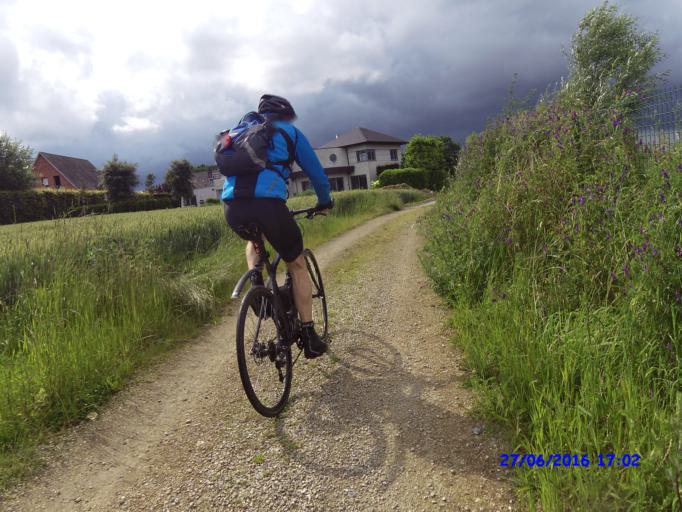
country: BE
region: Flanders
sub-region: Provincie Vlaams-Brabant
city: Ternat
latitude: 50.8416
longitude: 4.2006
